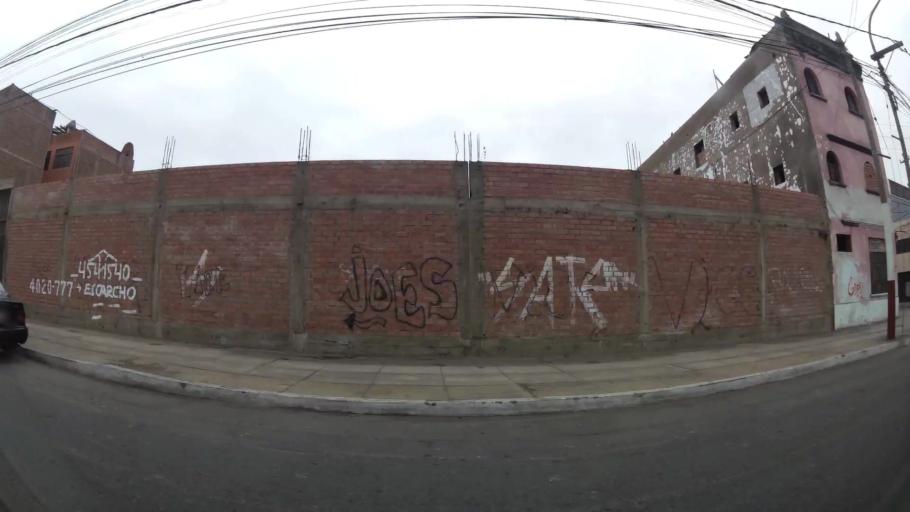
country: PE
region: Callao
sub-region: Callao
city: Callao
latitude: -12.0645
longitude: -77.1468
